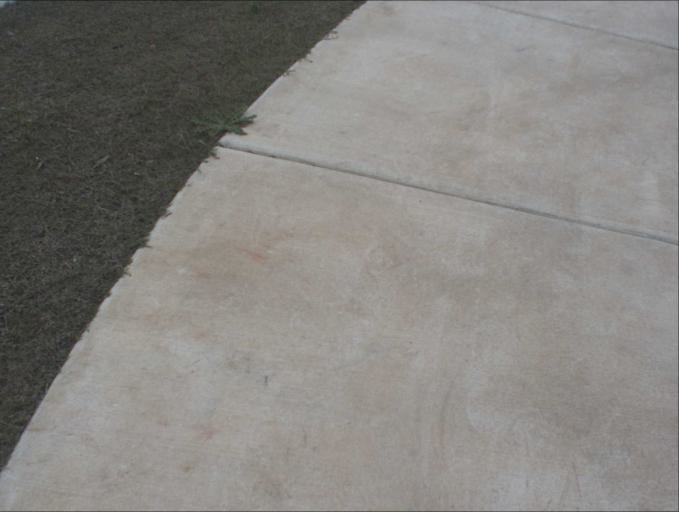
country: AU
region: Queensland
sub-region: Logan
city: Chambers Flat
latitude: -27.8040
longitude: 153.1114
